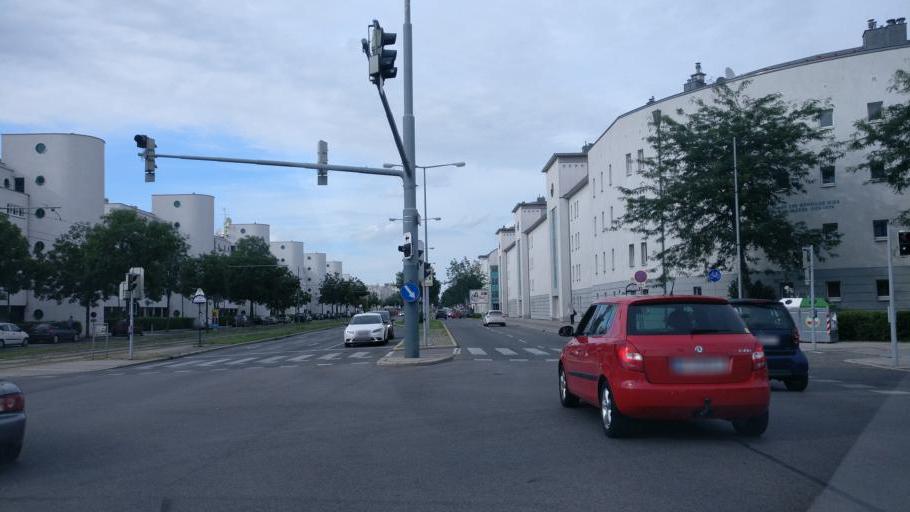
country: AT
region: Lower Austria
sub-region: Politischer Bezirk Korneuburg
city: Hagenbrunn
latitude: 48.2840
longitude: 16.4132
